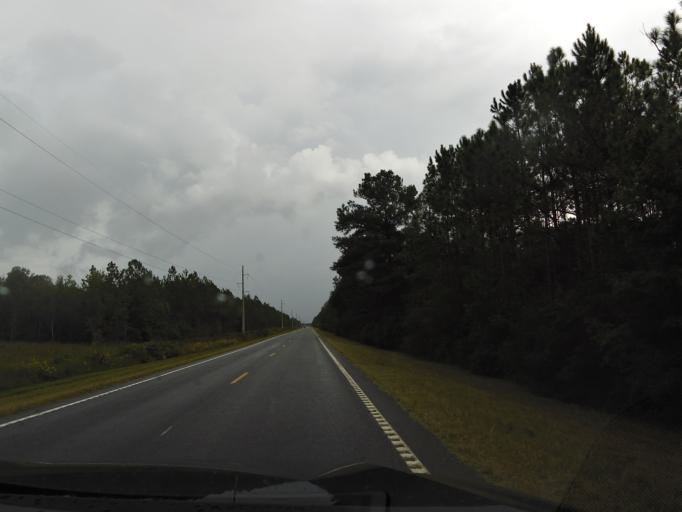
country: US
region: Florida
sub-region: Duval County
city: Baldwin
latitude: 30.4689
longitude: -82.0563
